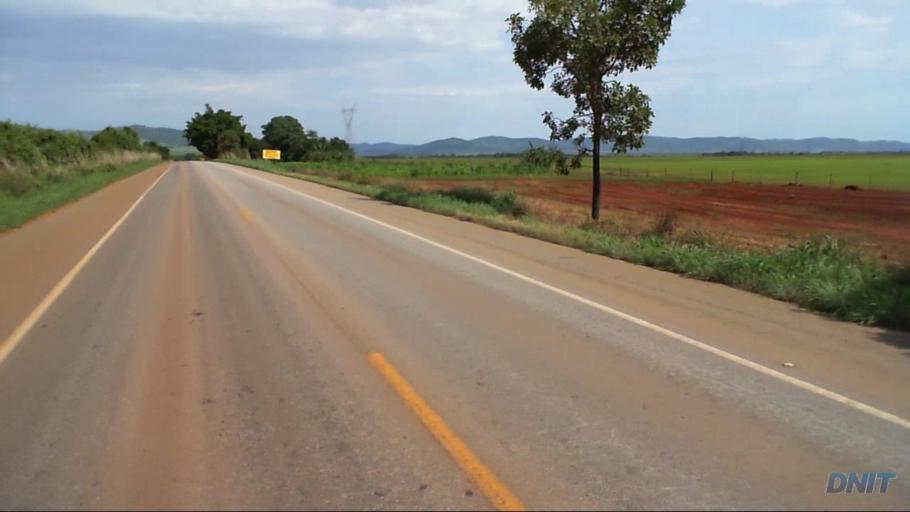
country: BR
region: Goias
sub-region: Barro Alto
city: Barro Alto
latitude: -15.0697
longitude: -48.8706
